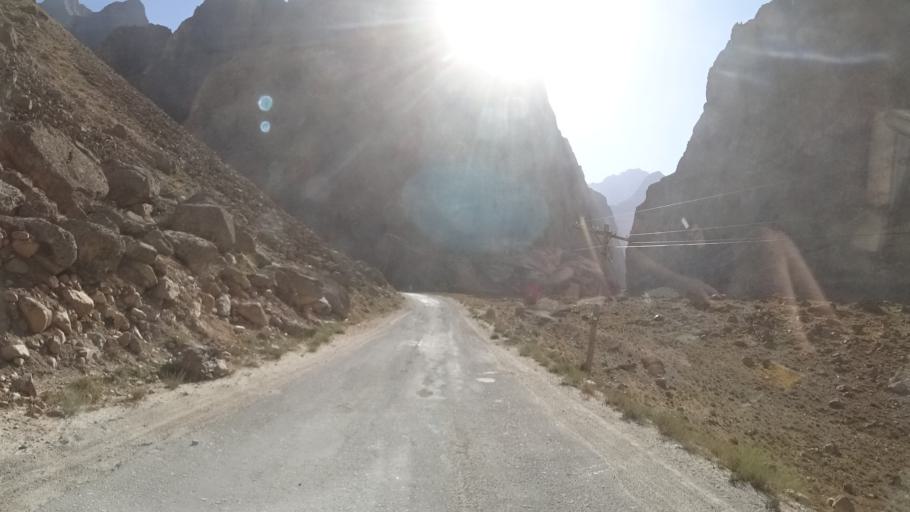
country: TJ
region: Gorno-Badakhshan
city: Rushon
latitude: 37.9926
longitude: 71.2737
